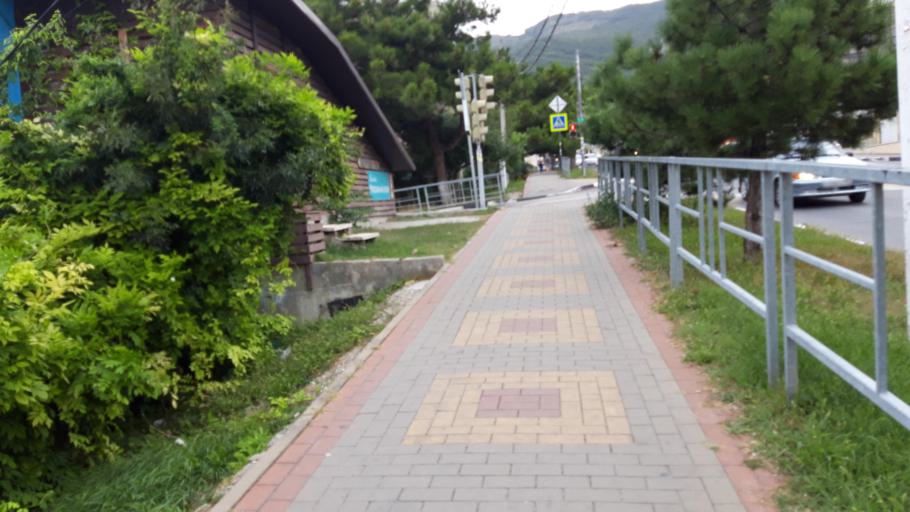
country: RU
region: Krasnodarskiy
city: Gelendzhik
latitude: 44.5670
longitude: 38.0885
